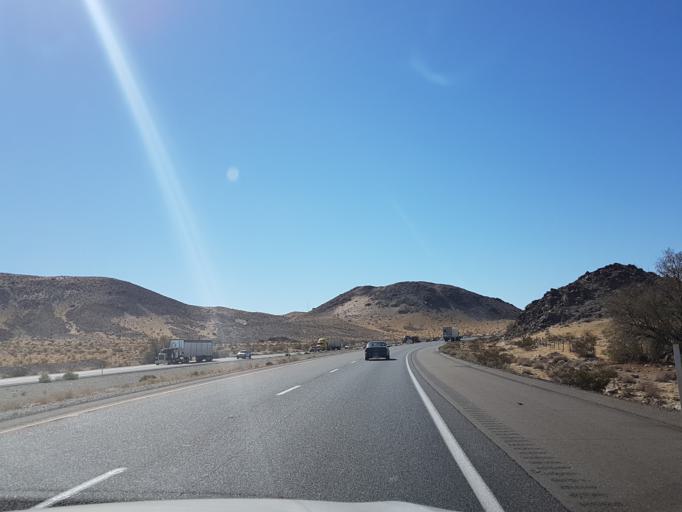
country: US
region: California
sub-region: San Bernardino County
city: Fort Irwin
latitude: 35.0808
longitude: -116.3846
